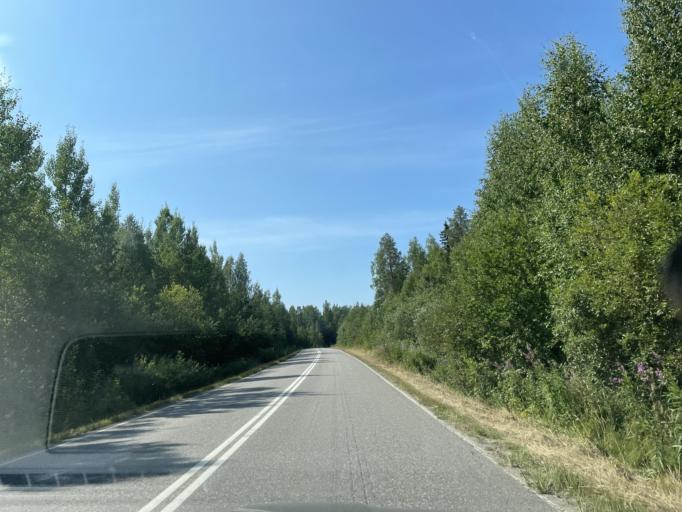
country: FI
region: Central Finland
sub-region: Saarijaervi-Viitasaari
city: Pihtipudas
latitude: 63.3634
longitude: 25.7281
